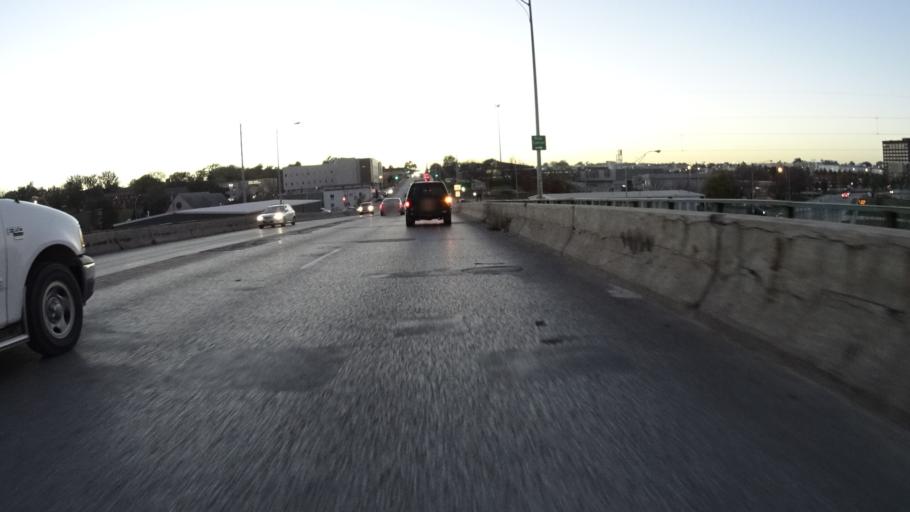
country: US
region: Nebraska
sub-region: Douglas County
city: Omaha
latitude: 41.2056
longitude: -95.9515
